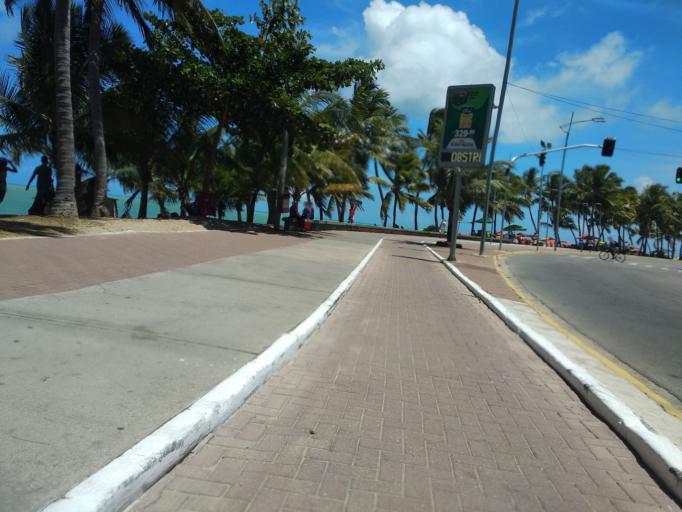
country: BR
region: Alagoas
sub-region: Maceio
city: Maceio
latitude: -9.6631
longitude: -35.6959
